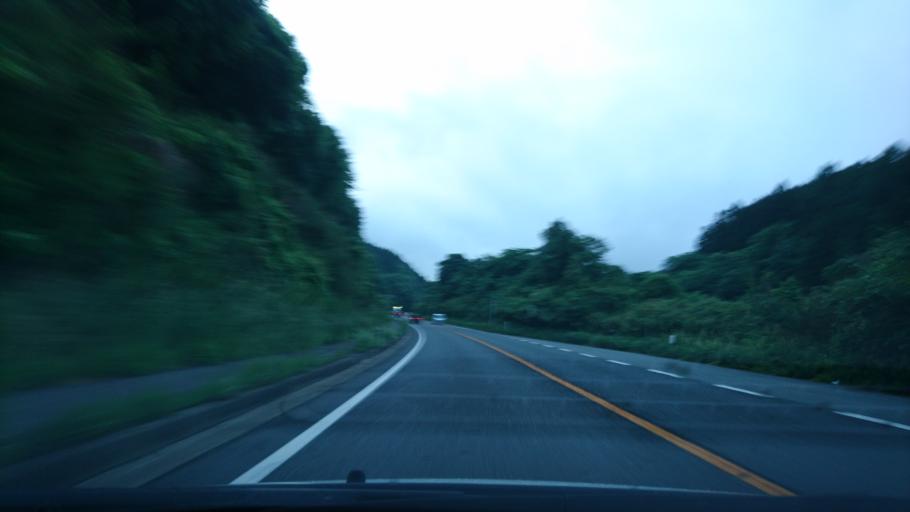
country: JP
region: Iwate
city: Ichinoseki
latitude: 38.8992
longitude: 141.1136
